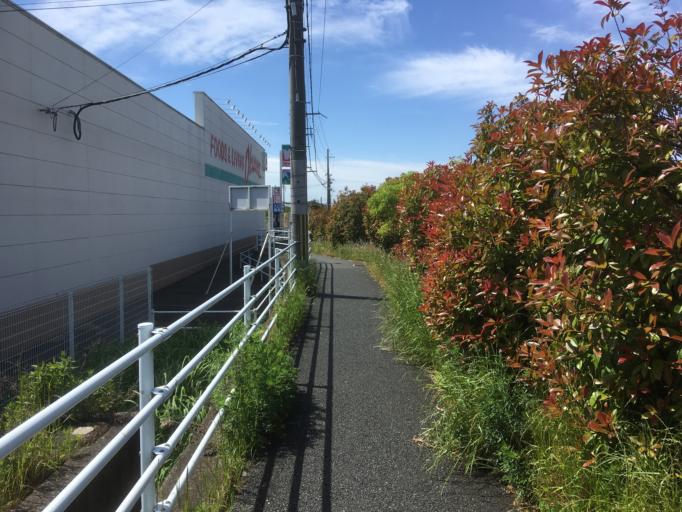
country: JP
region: Nara
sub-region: Ikoma-shi
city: Ikoma
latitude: 34.6801
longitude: 135.7063
